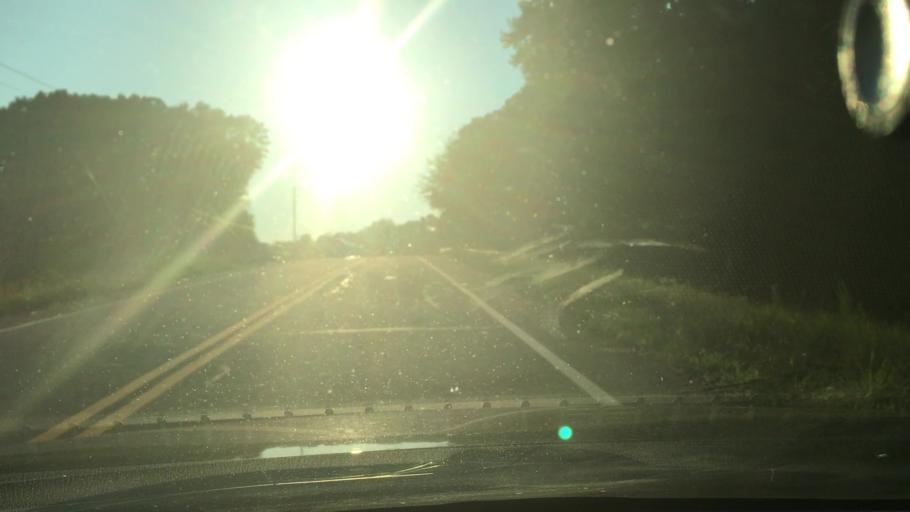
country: US
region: Georgia
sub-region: Coweta County
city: East Newnan
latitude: 33.3527
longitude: -84.7636
